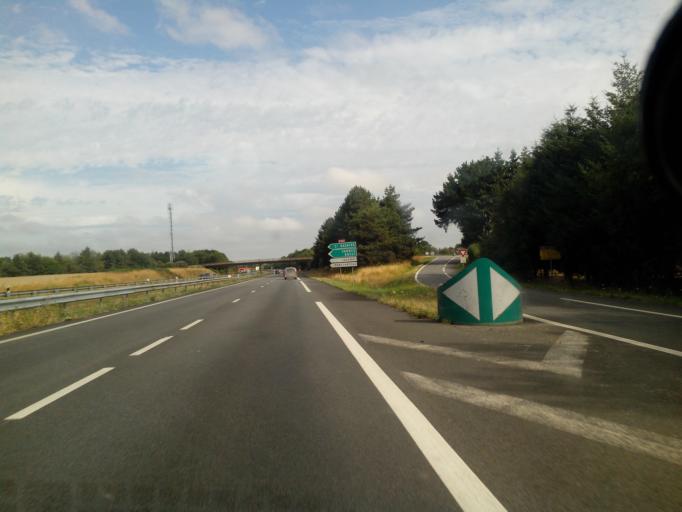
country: FR
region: Pays de la Loire
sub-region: Departement de la Loire-Atlantique
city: Le Temple-de-Bretagne
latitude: 47.3212
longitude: -1.7753
